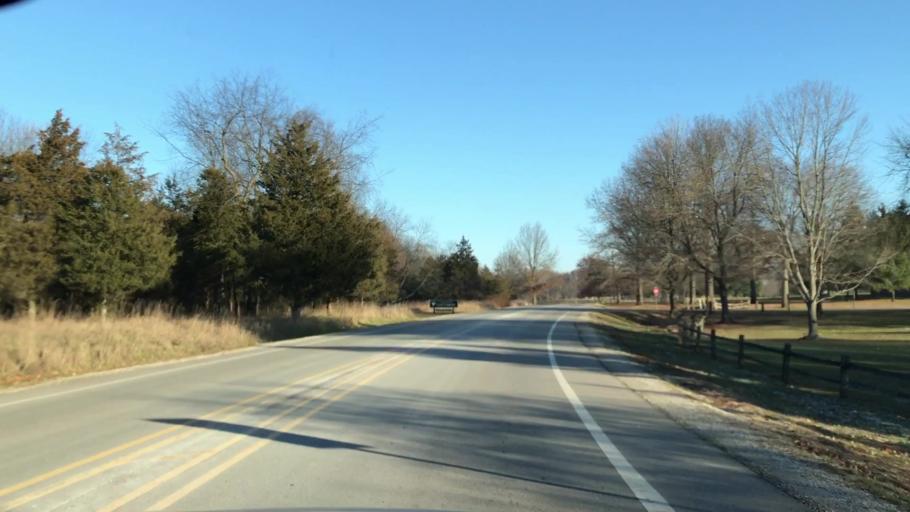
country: US
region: Michigan
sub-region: Oakland County
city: South Lyon
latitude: 42.5230
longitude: -83.6751
